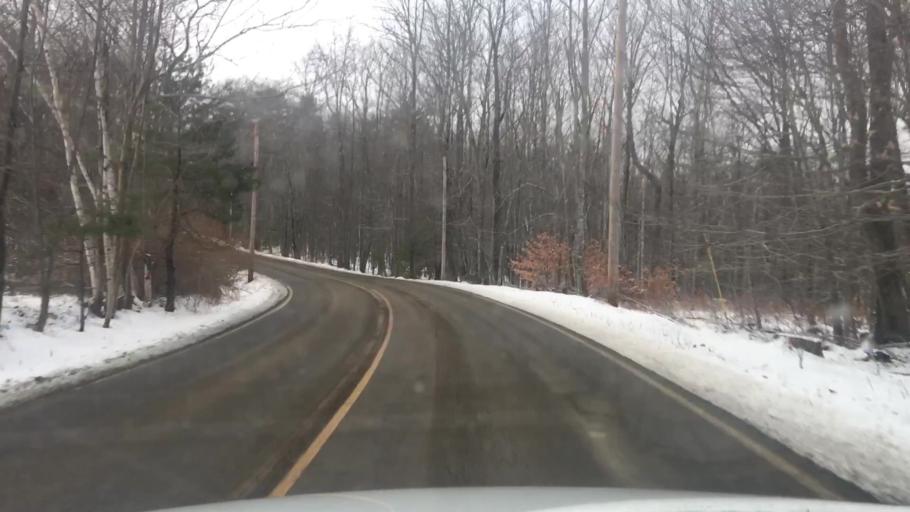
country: US
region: Maine
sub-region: Waldo County
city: Lincolnville
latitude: 44.2915
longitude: -69.0728
